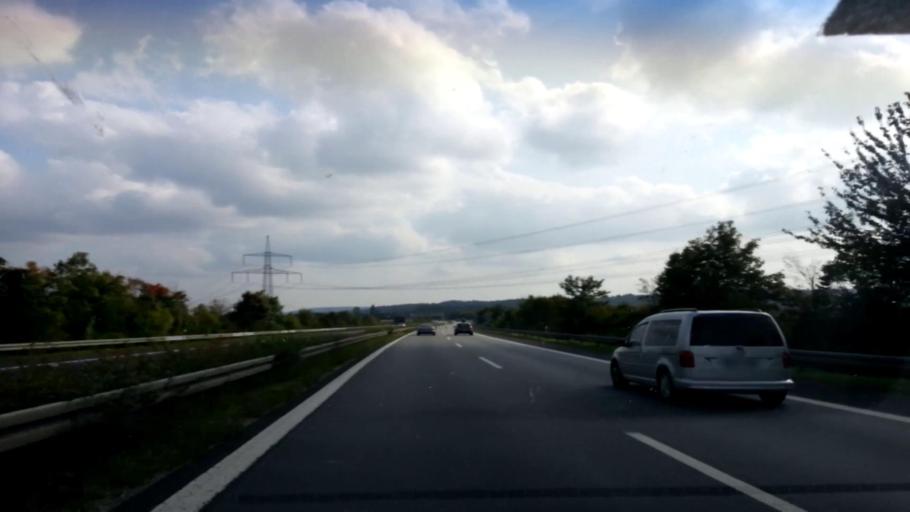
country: DE
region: Bavaria
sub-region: Upper Franconia
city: Viereth-Trunstadt
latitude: 49.9383
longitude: 10.7705
